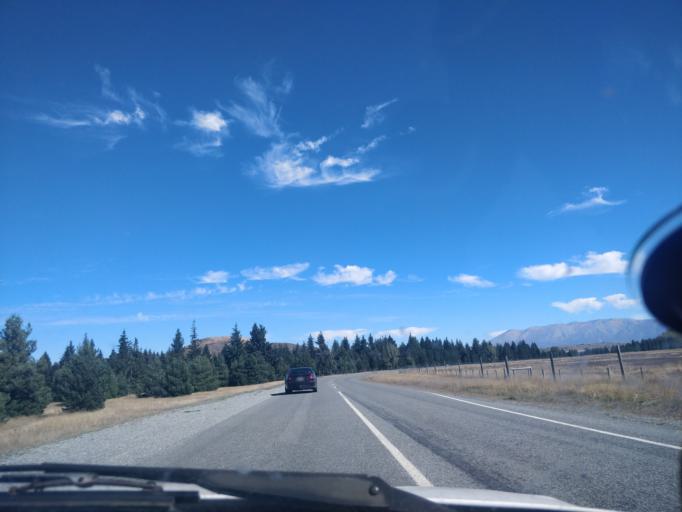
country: NZ
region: Otago
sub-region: Queenstown-Lakes District
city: Wanaka
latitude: -44.2711
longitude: 170.0617
